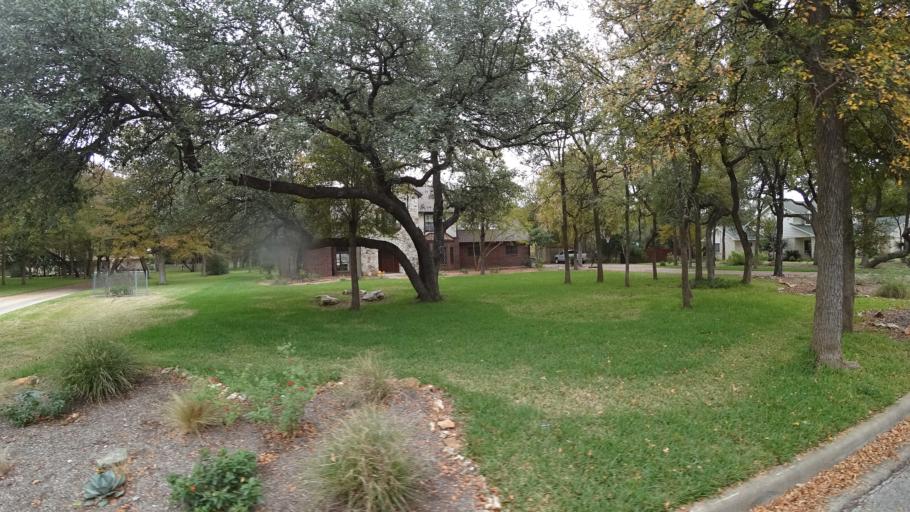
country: US
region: Texas
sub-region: Travis County
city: Wells Branch
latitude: 30.4359
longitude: -97.7150
